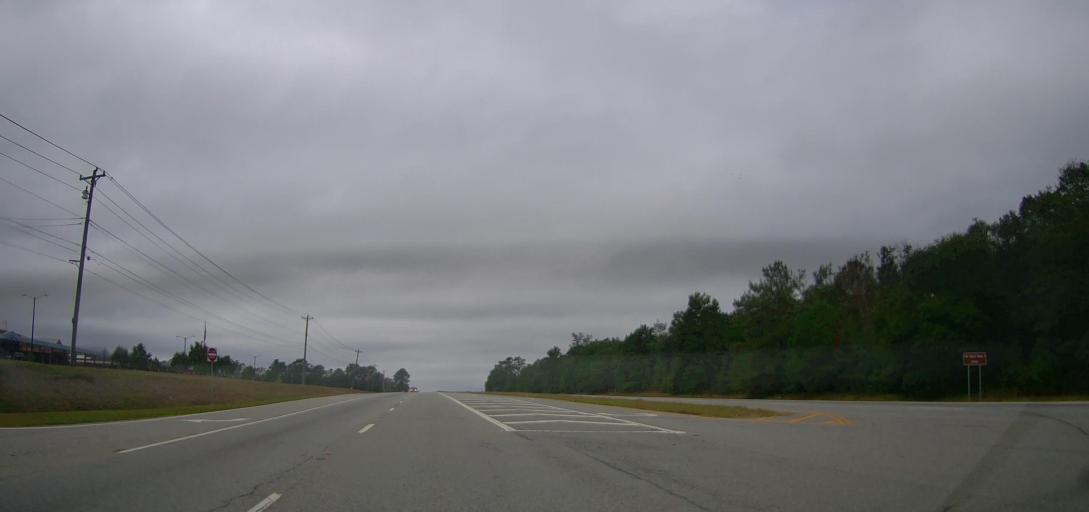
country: US
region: Georgia
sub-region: Thomas County
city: Thomasville
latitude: 30.8747
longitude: -83.9641
